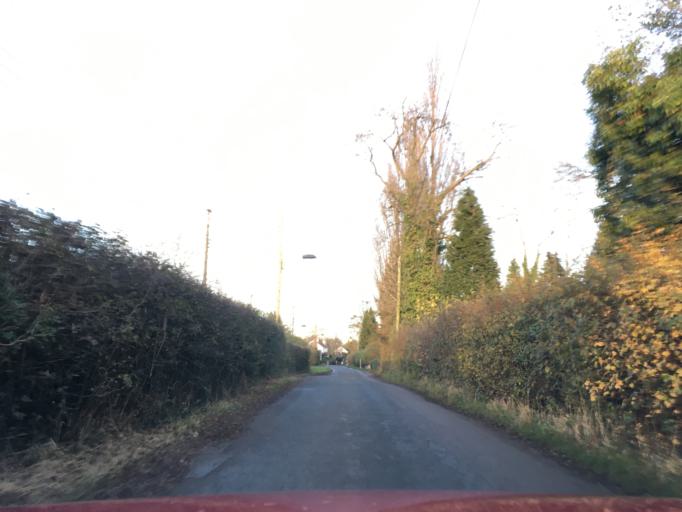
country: GB
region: England
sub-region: South Gloucestershire
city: Thornbury
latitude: 51.6152
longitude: -2.4999
